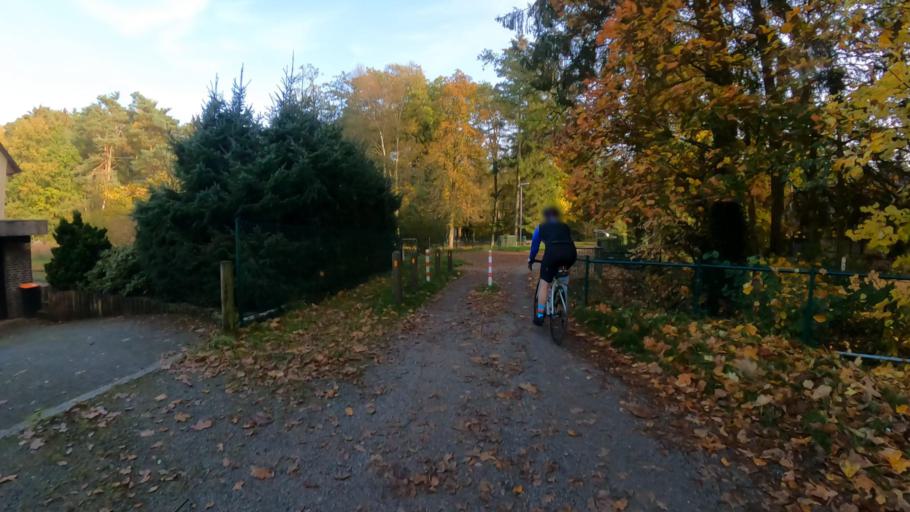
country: DE
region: Lower Saxony
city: Buchholz in der Nordheide
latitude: 53.3291
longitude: 9.8632
